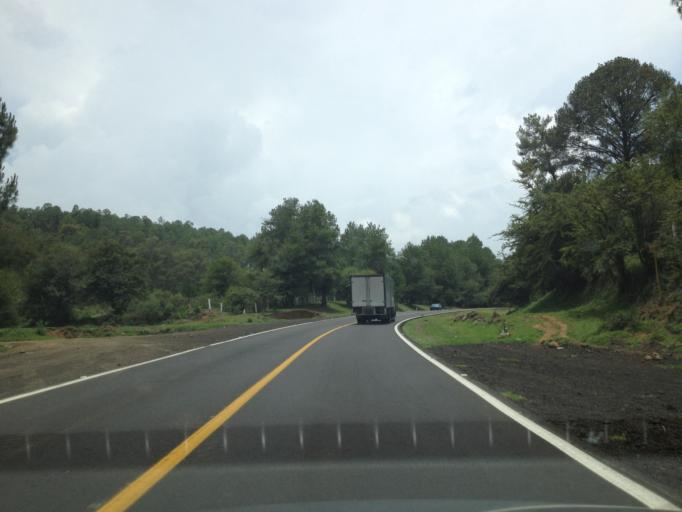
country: MX
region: Michoacan
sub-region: Patzcuaro
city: Santa Maria Huiramangaro (San Juan Tumbio)
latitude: 19.4967
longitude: -101.7719
